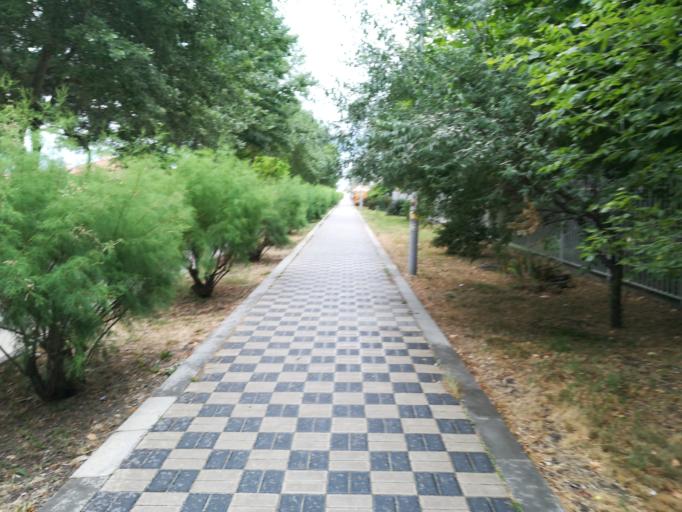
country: RU
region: Krasnodarskiy
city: Vityazevo
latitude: 44.9893
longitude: 37.2463
